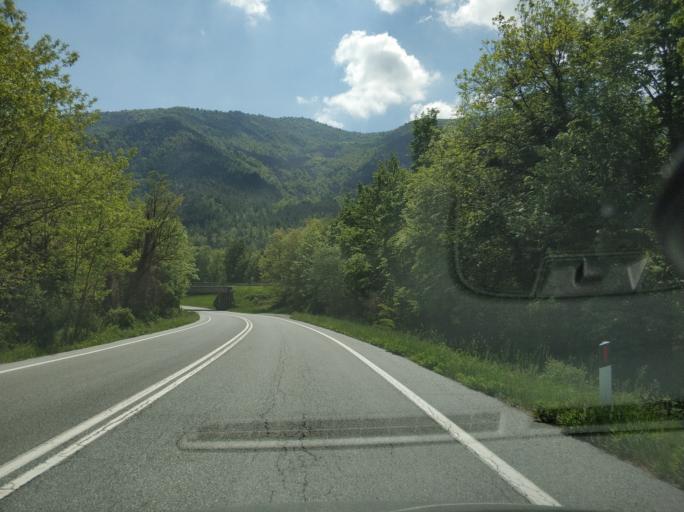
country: IT
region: Piedmont
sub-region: Provincia di Torino
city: Germagnano
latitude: 45.2585
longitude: 7.4620
